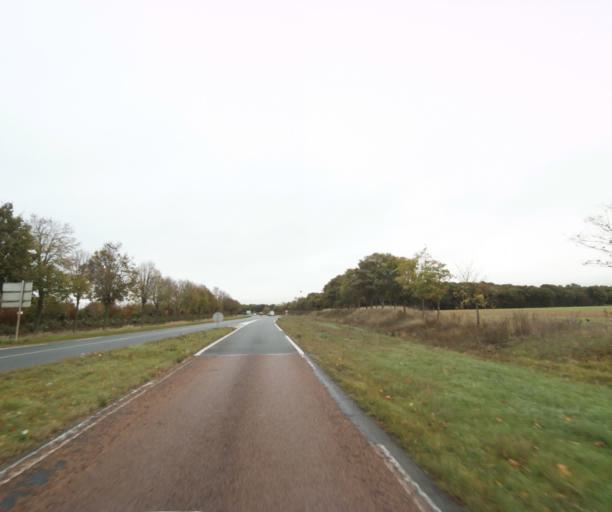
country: FR
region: Centre
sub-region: Departement d'Eure-et-Loir
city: Vernouillet
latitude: 48.7202
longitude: 1.3827
